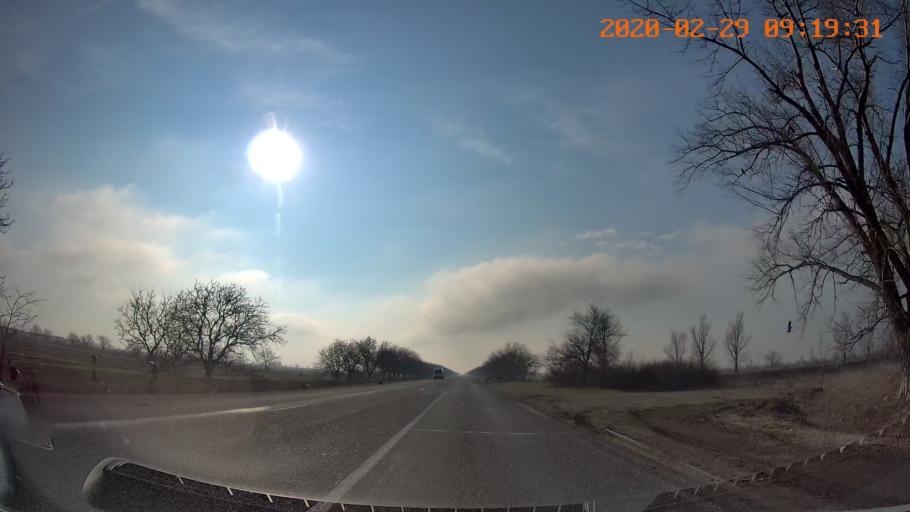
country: MD
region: Telenesti
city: Pervomaisc
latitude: 46.7616
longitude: 29.9398
